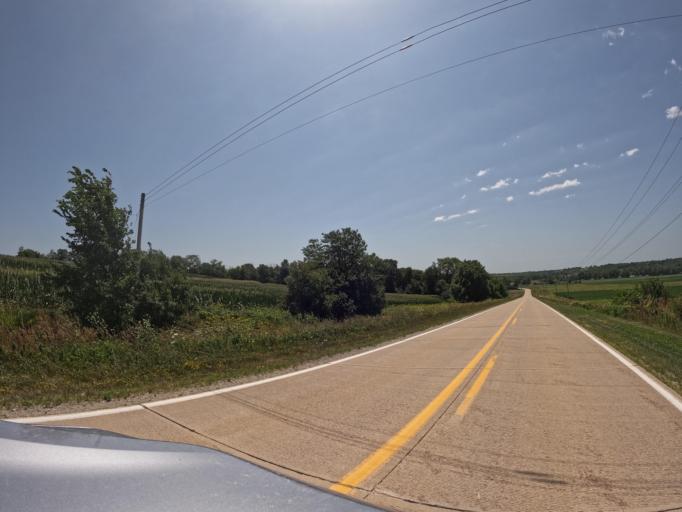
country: US
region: Iowa
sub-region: Henry County
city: Mount Pleasant
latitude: 40.9079
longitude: -91.5544
